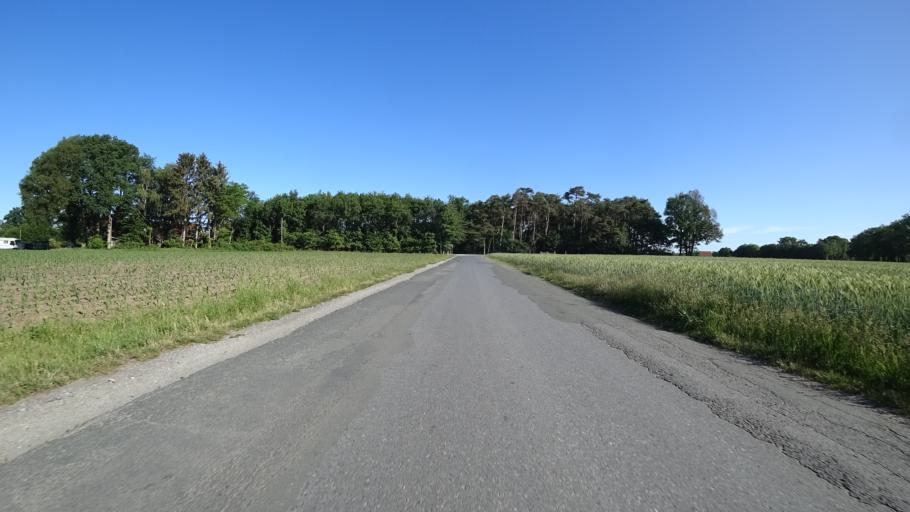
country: DE
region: North Rhine-Westphalia
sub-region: Regierungsbezirk Detmold
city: Guetersloh
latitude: 51.9157
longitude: 8.3250
